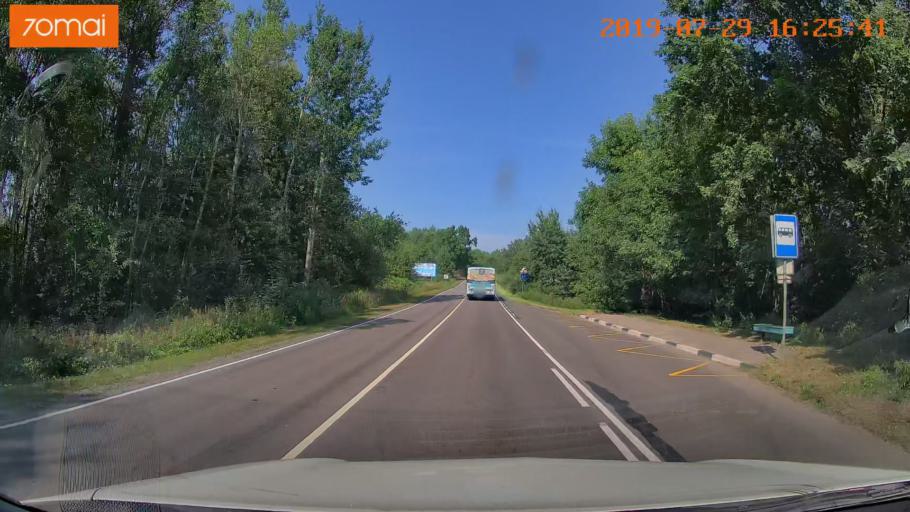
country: RU
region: Kaliningrad
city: Primorsk
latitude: 54.7247
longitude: 19.9685
